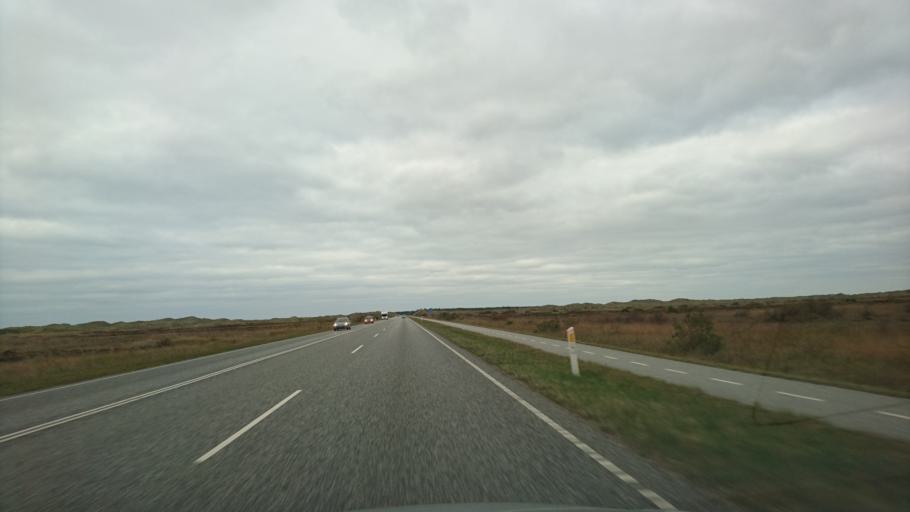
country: DK
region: North Denmark
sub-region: Frederikshavn Kommune
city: Skagen
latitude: 57.6841
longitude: 10.4659
